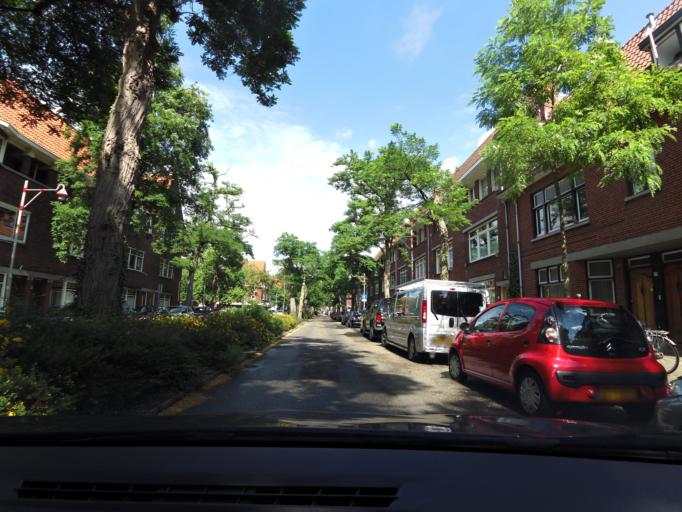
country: NL
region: South Holland
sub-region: Gemeente Den Haag
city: The Hague
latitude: 52.0928
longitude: 4.3256
